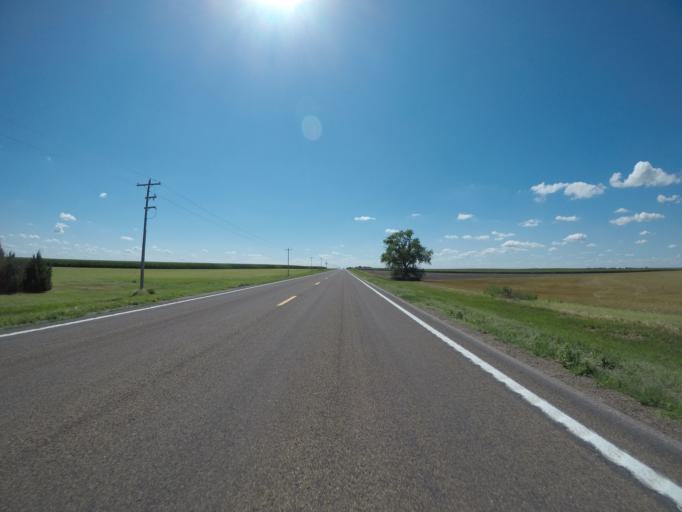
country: US
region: Nebraska
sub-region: Chase County
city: Imperial
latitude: 40.5376
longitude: -101.7882
